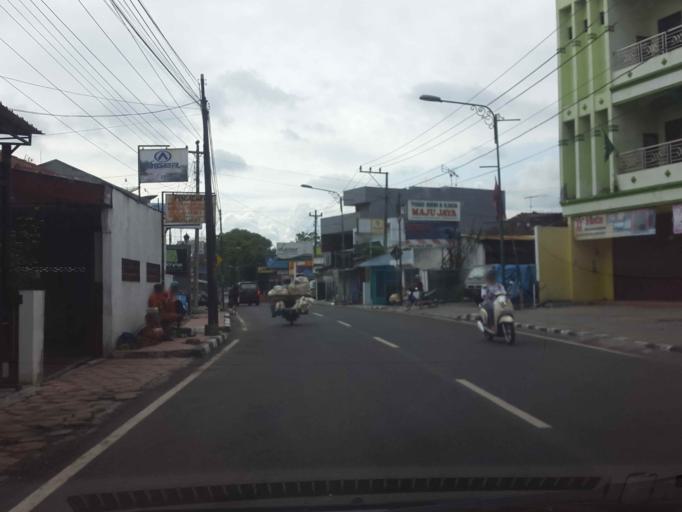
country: ID
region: Central Java
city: Salatiga
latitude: -7.3227
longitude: 110.4969
